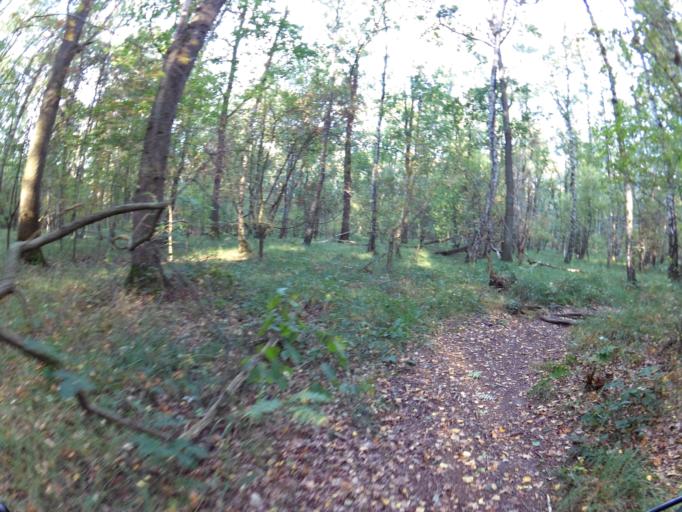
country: DE
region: North Rhine-Westphalia
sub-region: Regierungsbezirk Koln
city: Gangelt
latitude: 50.9679
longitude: 6.0130
